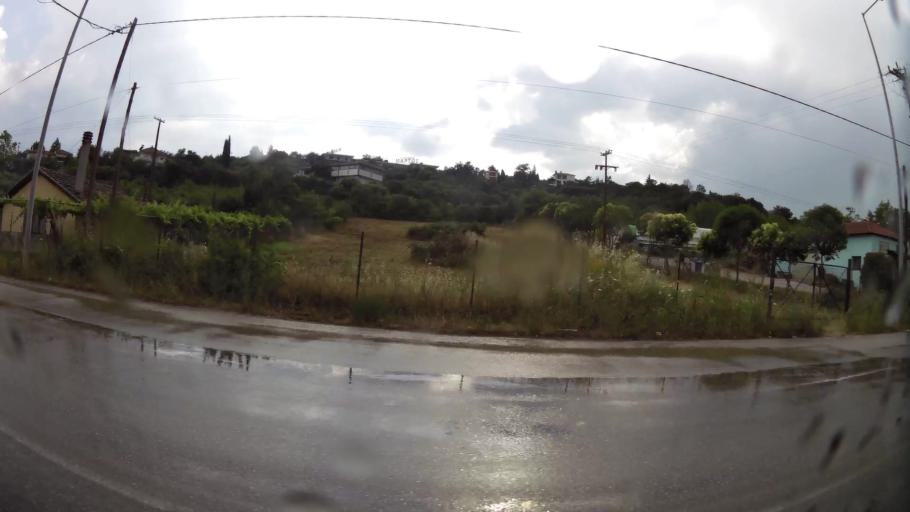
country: GR
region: Central Macedonia
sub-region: Nomos Imathias
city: Veroia
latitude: 40.5403
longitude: 22.1966
